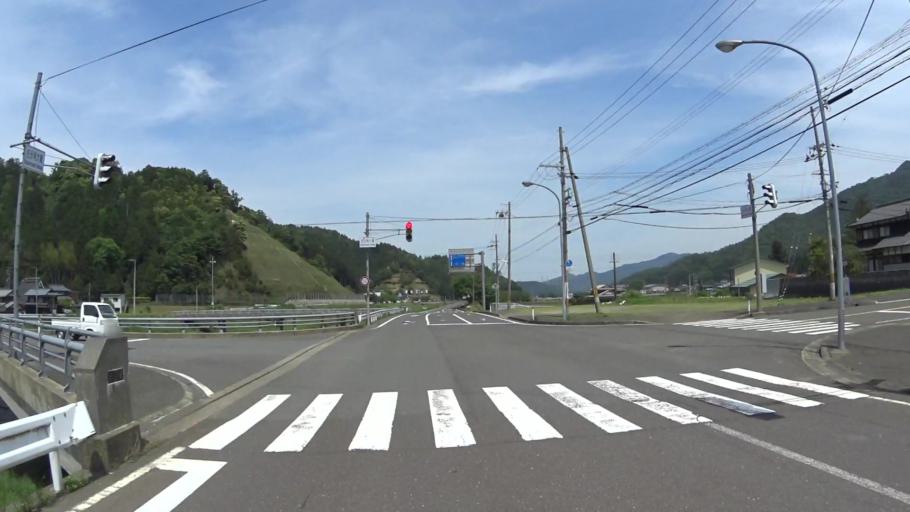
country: JP
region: Fukui
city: Obama
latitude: 35.4506
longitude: 135.5607
